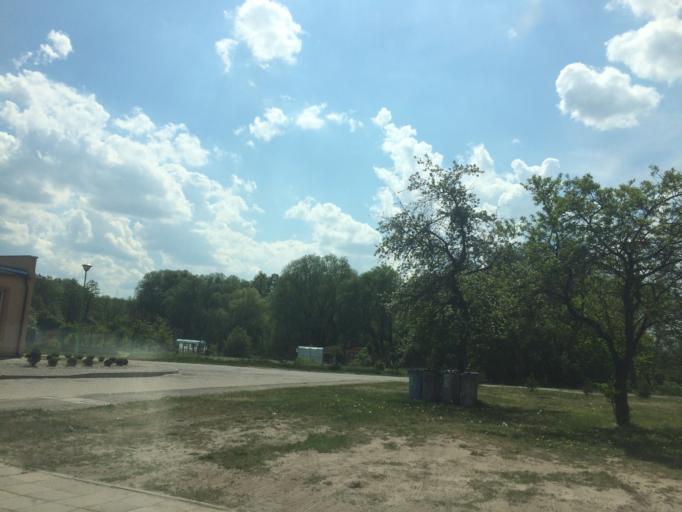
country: PL
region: Warmian-Masurian Voivodeship
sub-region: Powiat nowomiejski
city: Nowe Miasto Lubawskie
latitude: 53.4411
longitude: 19.6043
